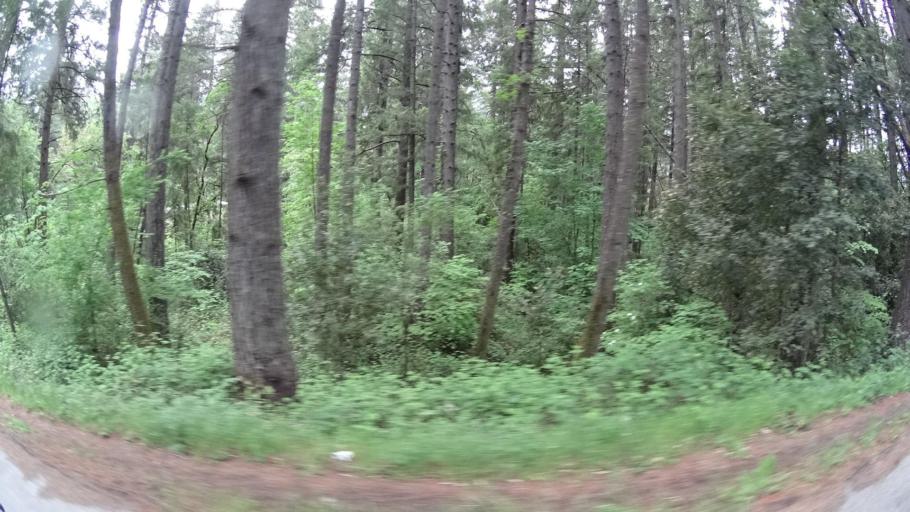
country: US
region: California
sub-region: Humboldt County
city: Willow Creek
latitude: 41.0531
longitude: -123.6709
